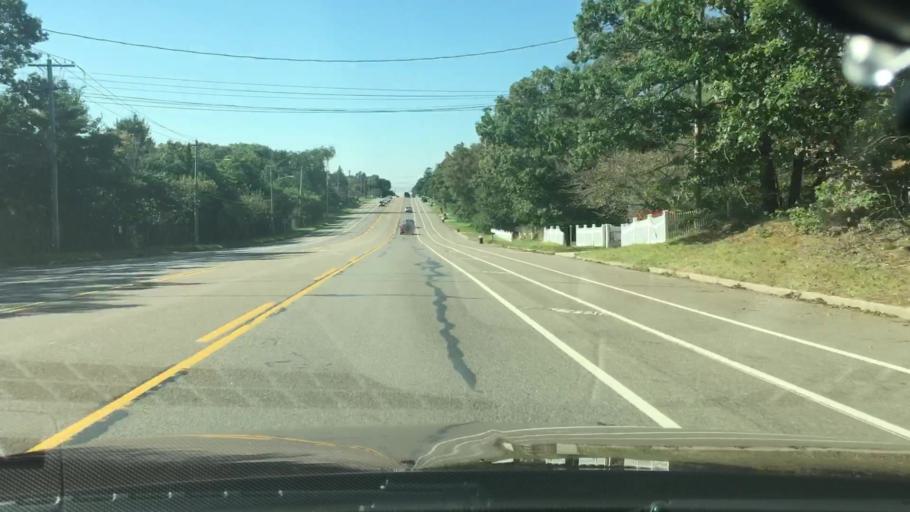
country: US
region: New York
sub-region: Suffolk County
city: North Patchogue
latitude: 40.7952
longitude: -72.9935
